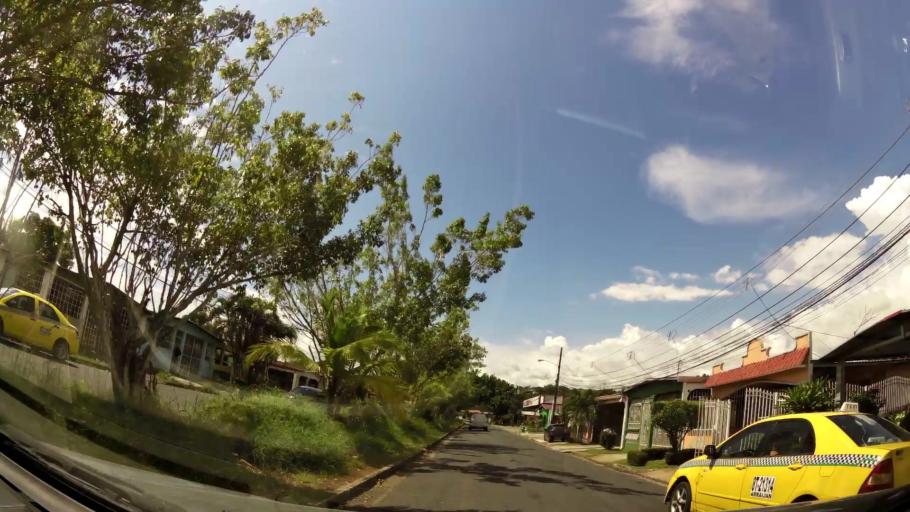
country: PA
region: Panama
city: Nuevo Arraijan
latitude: 8.9142
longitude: -79.7100
